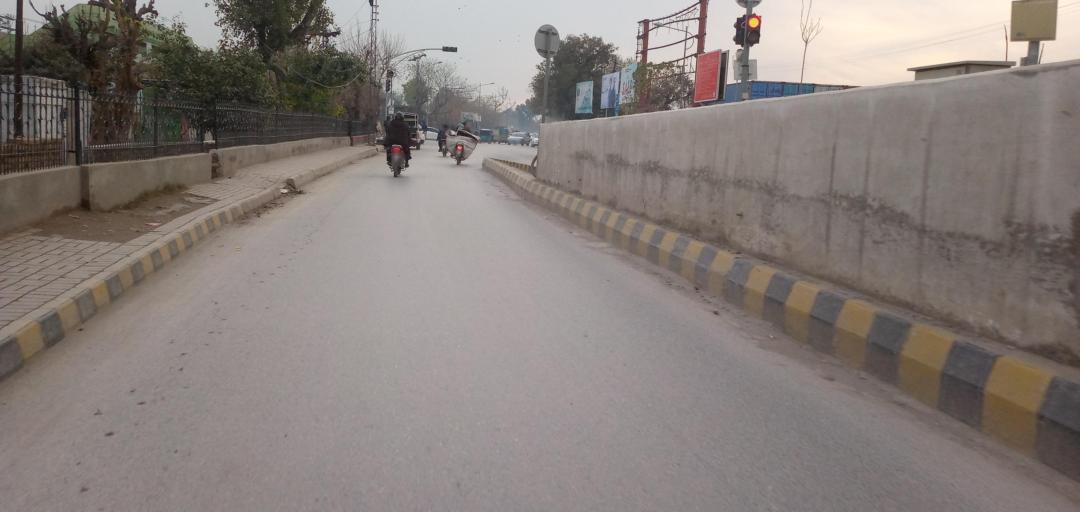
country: PK
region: Khyber Pakhtunkhwa
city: Peshawar
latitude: 34.0017
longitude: 71.5525
